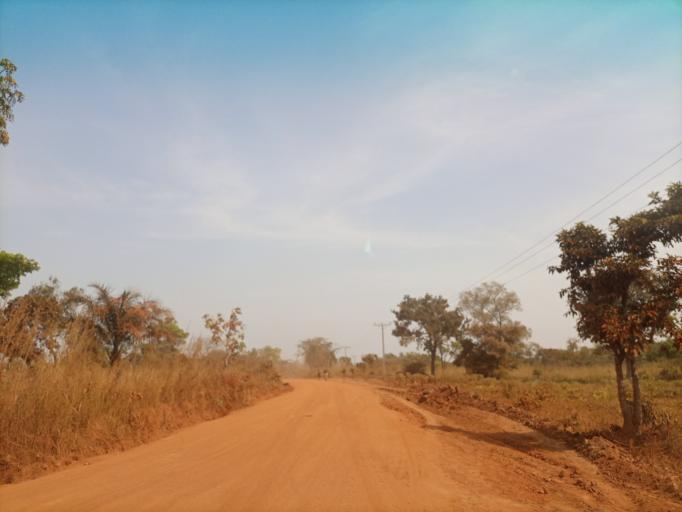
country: NG
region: Enugu
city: Eha Amufu
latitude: 6.6691
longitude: 7.7425
